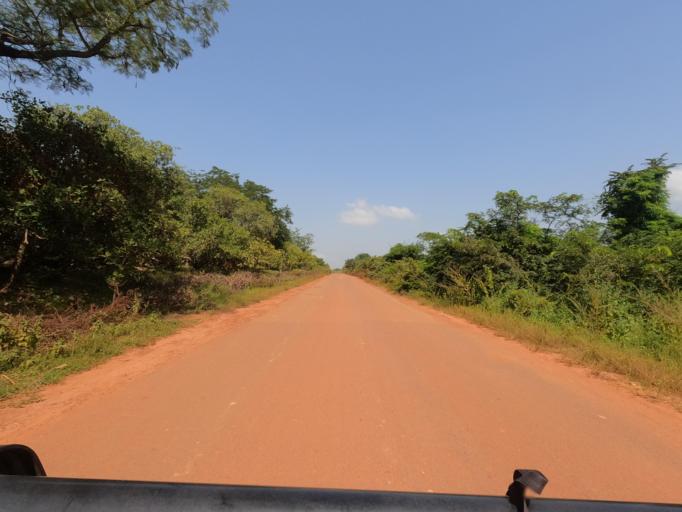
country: GW
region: Cacheu
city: Canchungo
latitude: 12.2660
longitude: -15.7863
